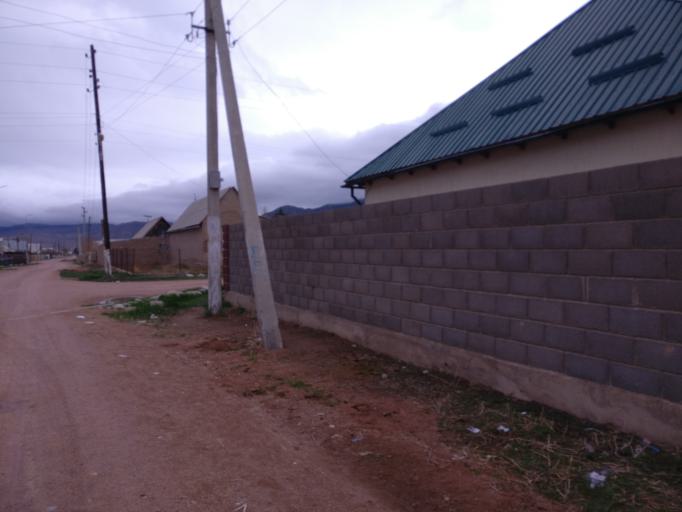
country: KG
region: Ysyk-Koel
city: Bokombayevskoye
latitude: 42.1083
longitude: 76.9804
